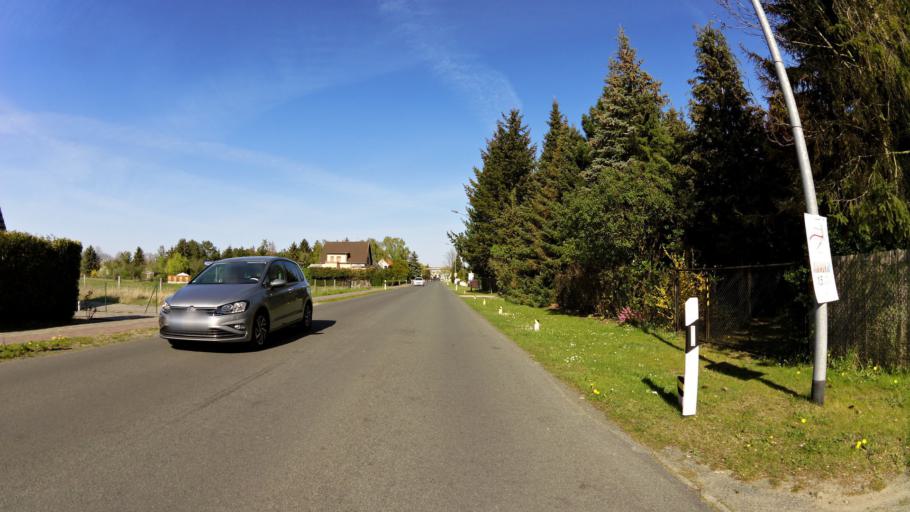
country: DE
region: Saxony-Anhalt
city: Stendal
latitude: 52.5859
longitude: 11.8315
